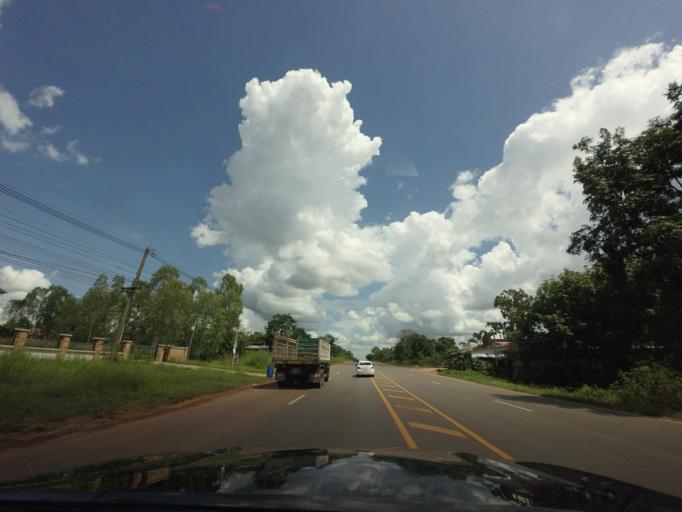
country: TH
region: Changwat Udon Thani
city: Ban Dung
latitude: 17.6847
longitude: 103.2097
